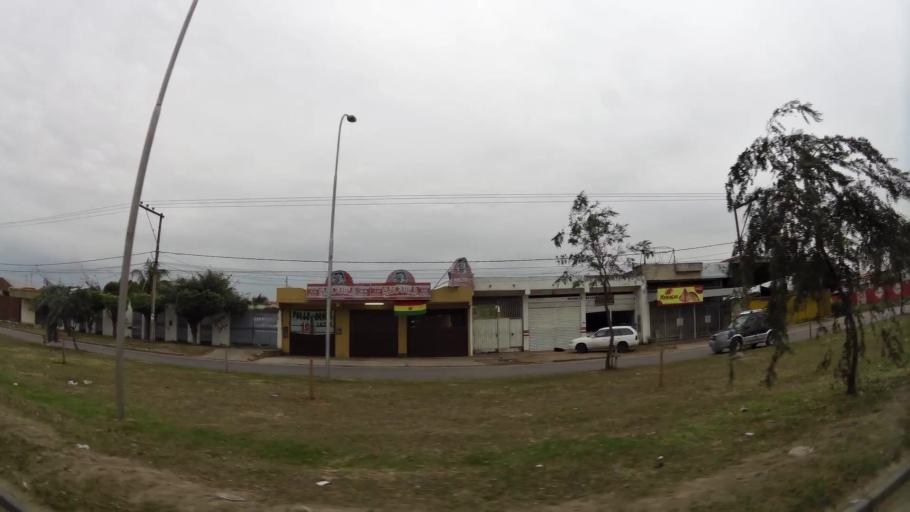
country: BO
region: Santa Cruz
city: Santa Cruz de la Sierra
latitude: -17.8274
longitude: -63.1766
